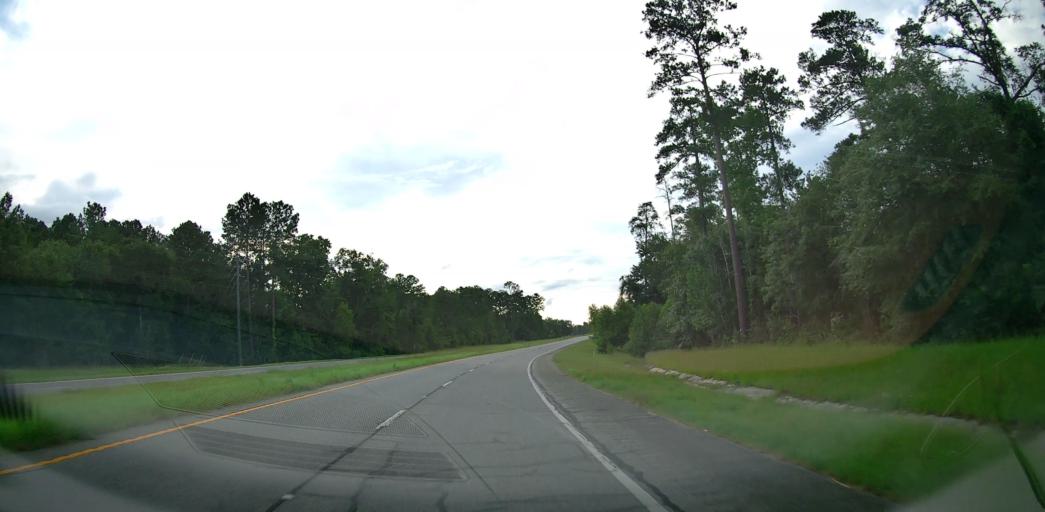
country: US
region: Georgia
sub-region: Pulaski County
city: Hawkinsville
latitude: 32.2632
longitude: -83.4087
